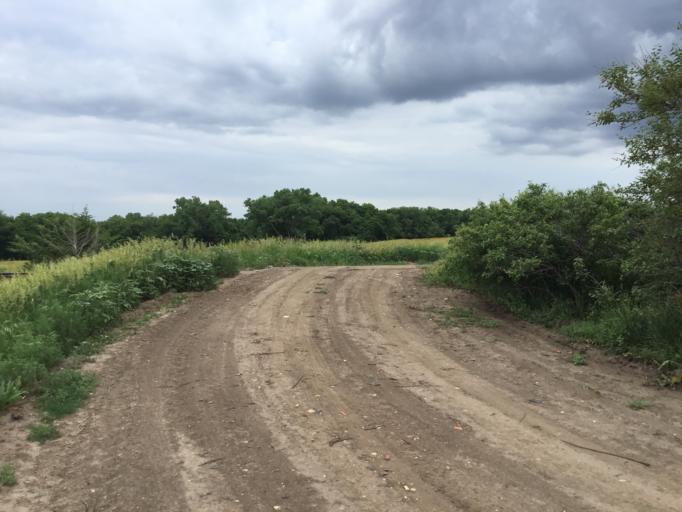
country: US
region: Kansas
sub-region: Republic County
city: Belleville
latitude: 39.8336
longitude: -97.5965
